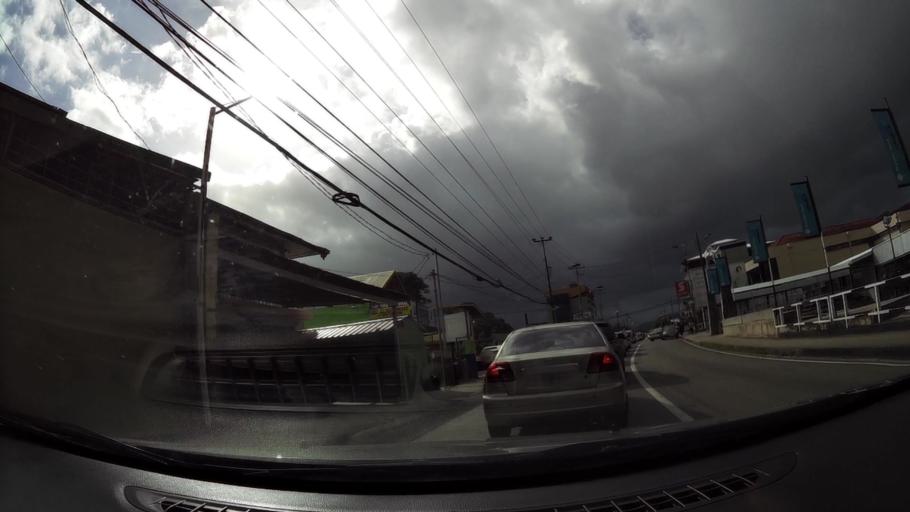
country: TT
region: Tunapuna/Piarco
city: Tunapuna
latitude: 10.6449
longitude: -61.3951
